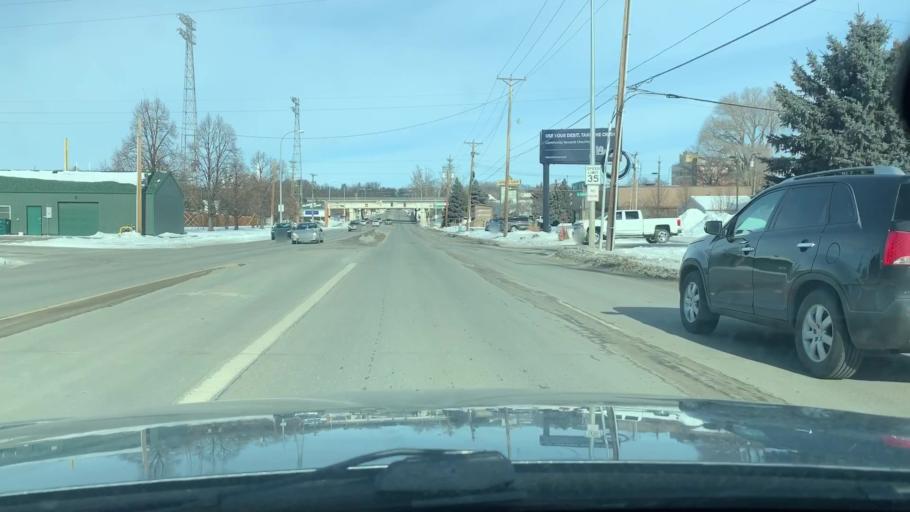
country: US
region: North Dakota
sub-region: Burleigh County
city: Bismarck
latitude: 46.8029
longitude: -100.7944
